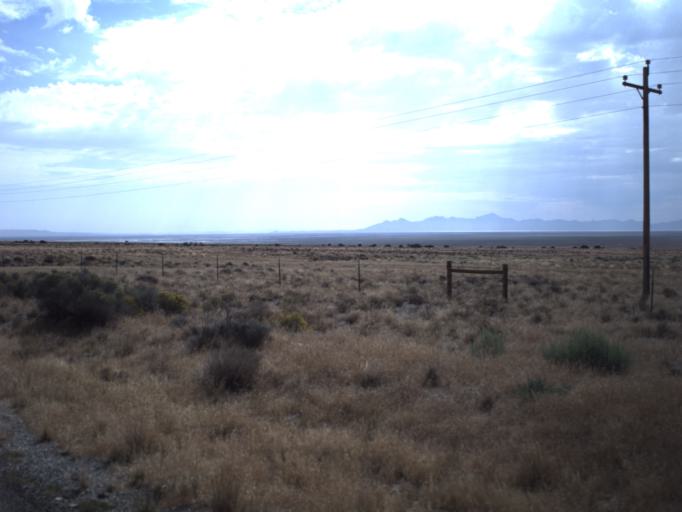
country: US
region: Utah
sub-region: Tooele County
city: Wendover
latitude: 41.4336
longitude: -113.7742
